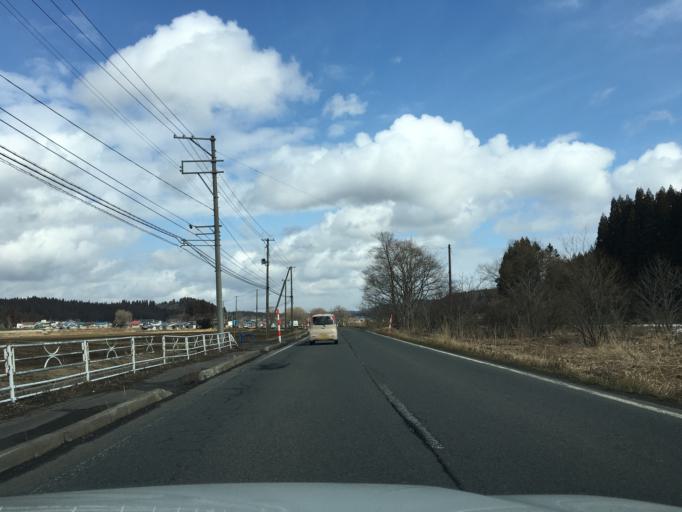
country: JP
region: Akita
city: Takanosu
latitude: 40.0381
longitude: 140.2781
